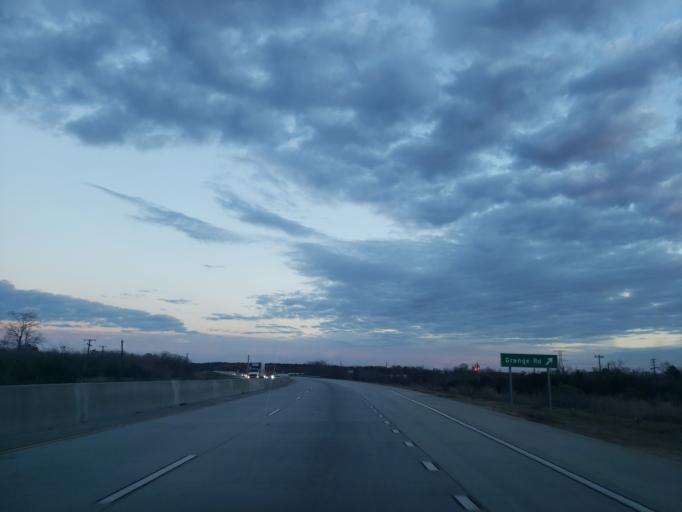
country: US
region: Georgia
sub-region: Chatham County
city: Garden City
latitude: 32.1303
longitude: -81.1641
